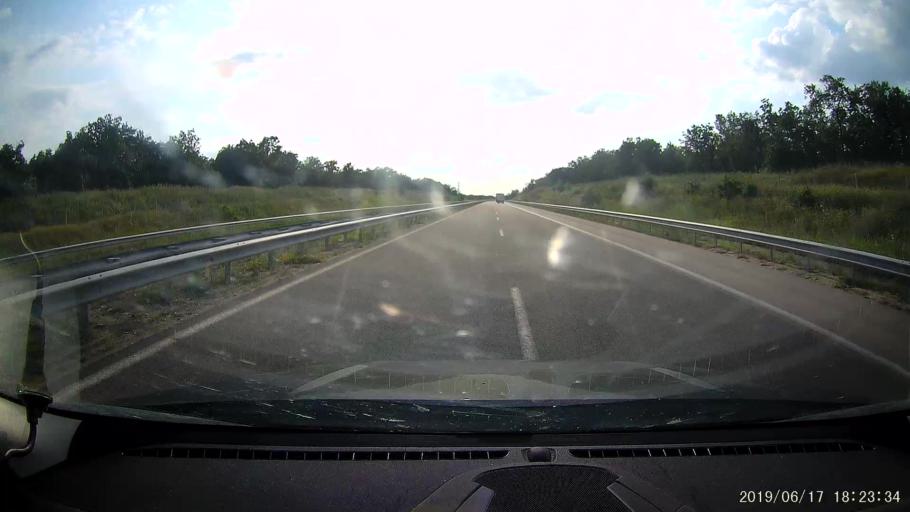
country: BG
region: Khaskovo
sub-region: Obshtina Simeonovgrad
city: Simeonovgrad
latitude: 41.9764
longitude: 25.7171
